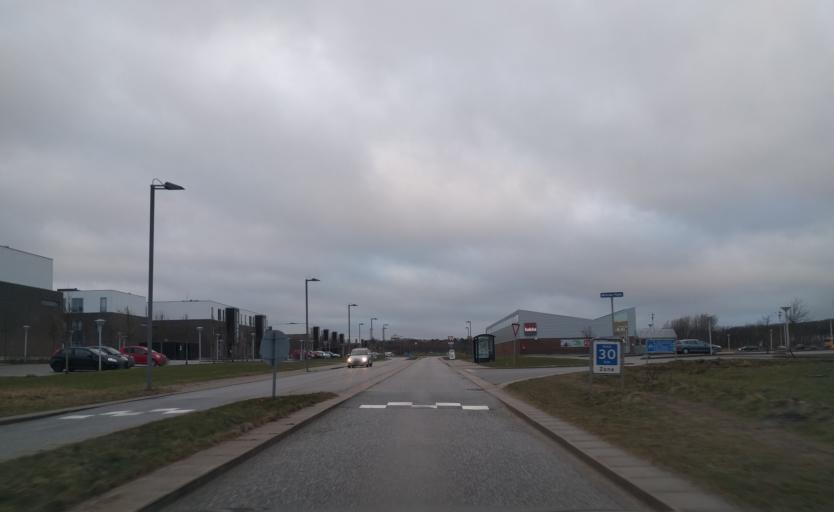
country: DK
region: North Denmark
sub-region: Alborg Kommune
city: Gistrup
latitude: 57.0130
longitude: 9.9689
